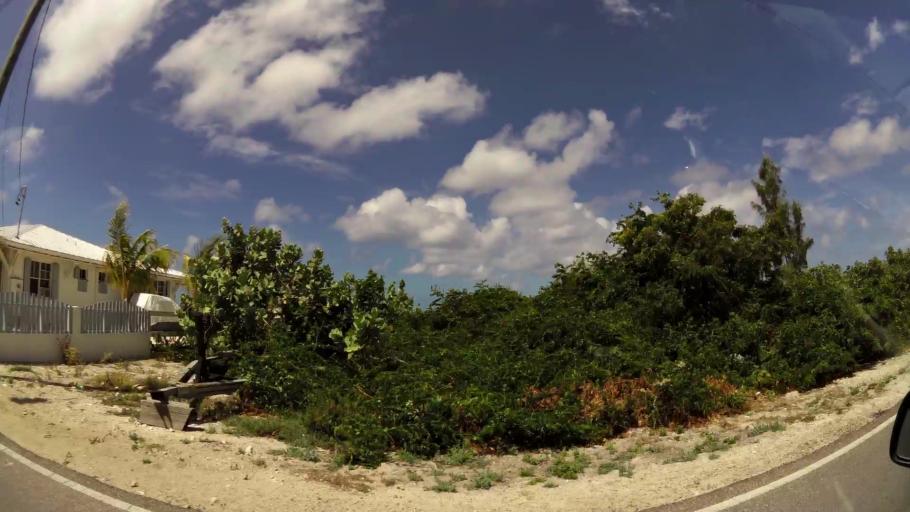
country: TC
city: Cockburn Town
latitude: 21.4776
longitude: -71.1488
